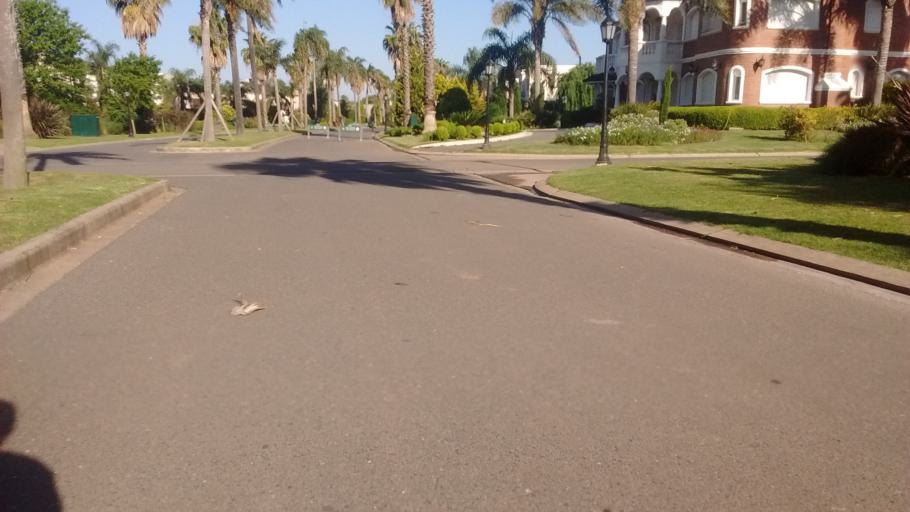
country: AR
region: Santa Fe
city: Funes
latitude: -32.9268
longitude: -60.8250
